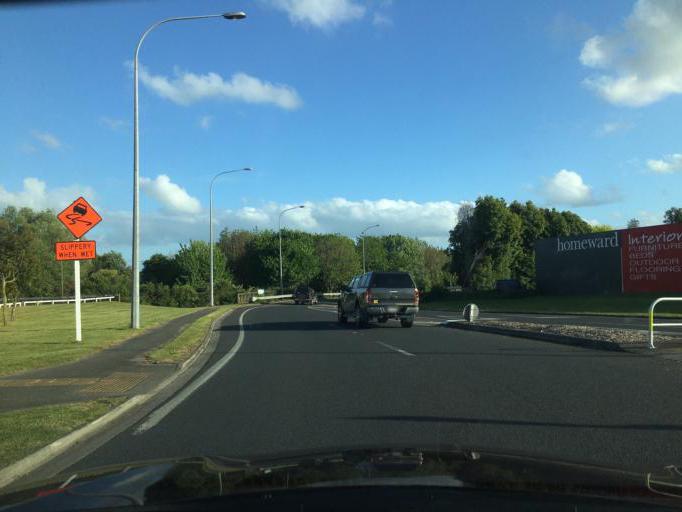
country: NZ
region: Waikato
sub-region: Waipa District
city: Cambridge
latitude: -38.0076
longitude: 175.3302
